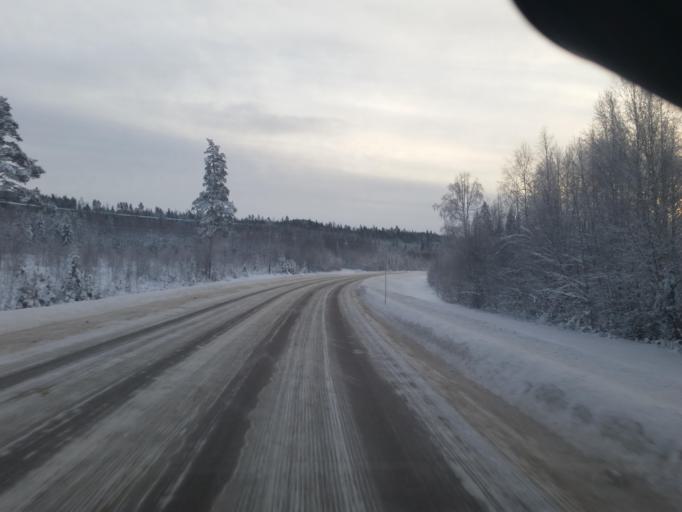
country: SE
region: Norrbotten
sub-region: Alvsbyns Kommun
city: AElvsbyn
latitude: 65.6739
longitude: 21.2124
